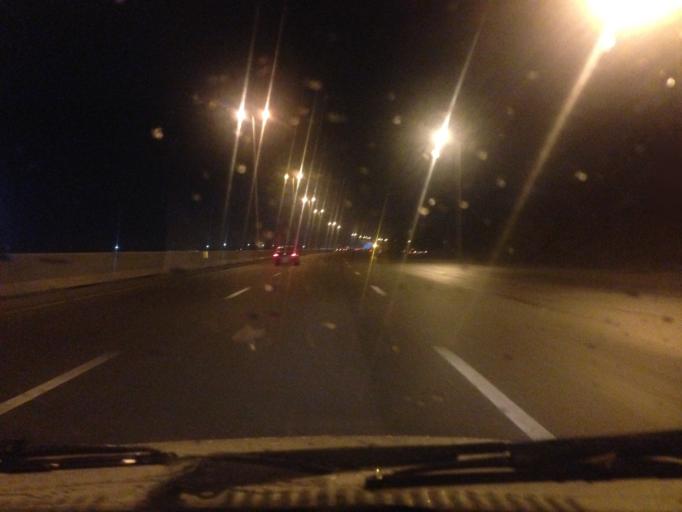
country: IR
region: Tehran
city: Eslamshahr
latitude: 35.4406
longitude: 51.2050
